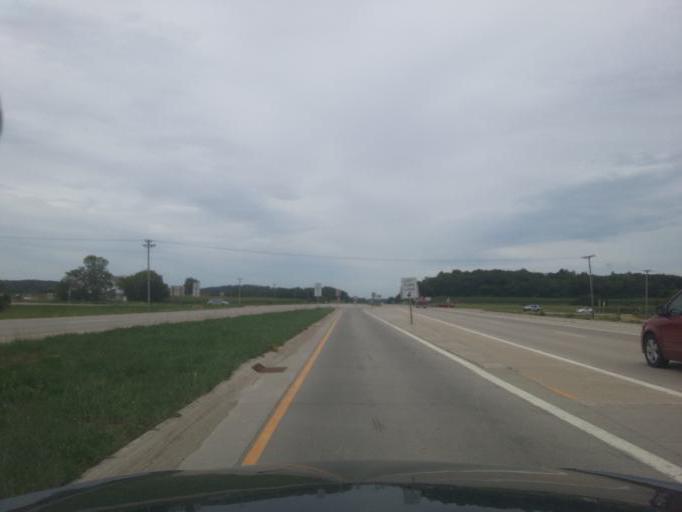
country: US
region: Wisconsin
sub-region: Dane County
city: McFarland
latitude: 43.0410
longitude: -89.2485
